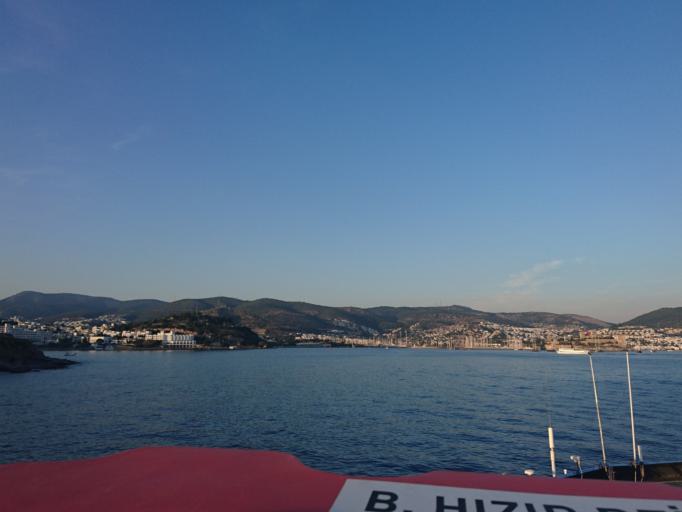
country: TR
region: Mugla
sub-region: Bodrum
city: Bodrum
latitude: 37.0208
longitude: 27.4201
